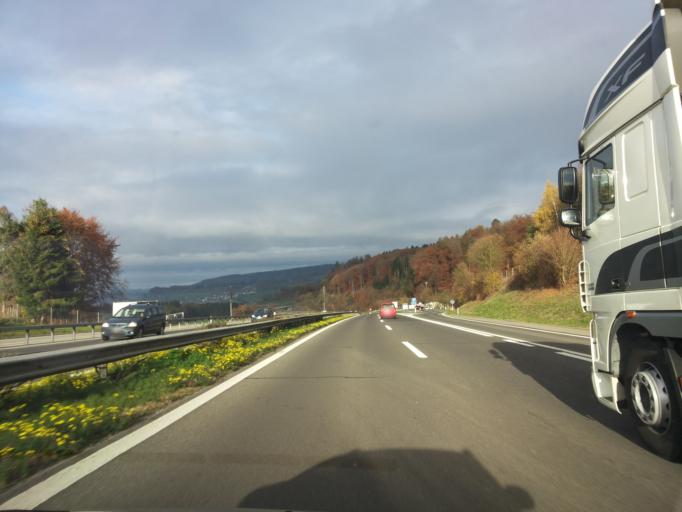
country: CH
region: Lucerne
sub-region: Sursee District
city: Knutwil
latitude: 47.1950
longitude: 8.0692
